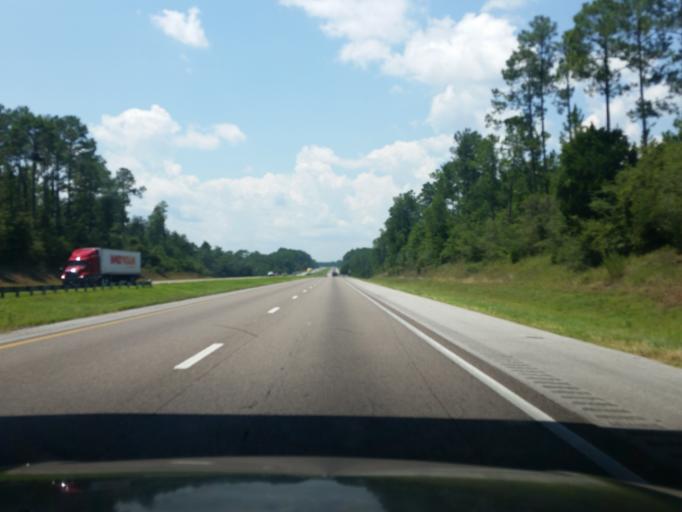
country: US
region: Alabama
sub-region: Baldwin County
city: Robertsdale
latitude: 30.6009
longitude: -87.5540
